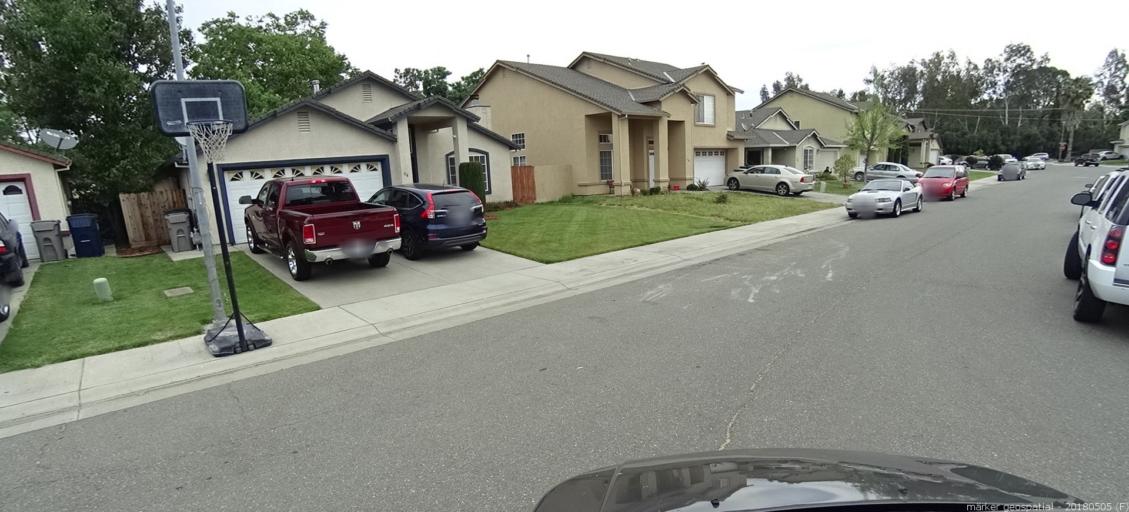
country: US
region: California
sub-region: Sacramento County
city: Rio Linda
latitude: 38.6590
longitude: -121.4460
